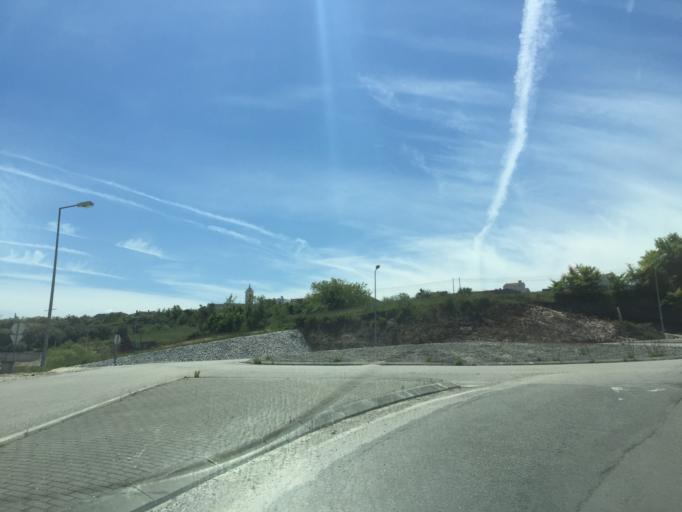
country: PT
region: Leiria
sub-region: Pombal
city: Lourical
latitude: 40.0668
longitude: -8.7287
